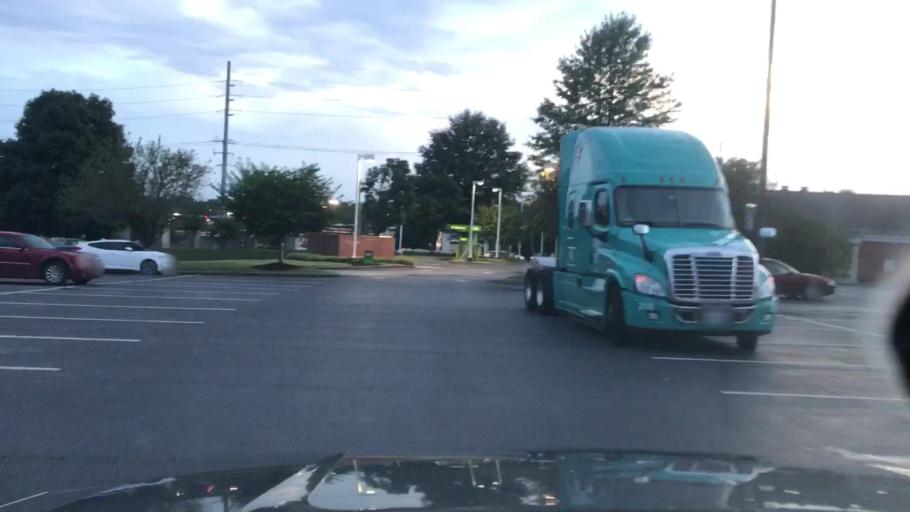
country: US
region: Tennessee
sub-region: Rutherford County
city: La Vergne
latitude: 36.0880
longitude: -86.6479
